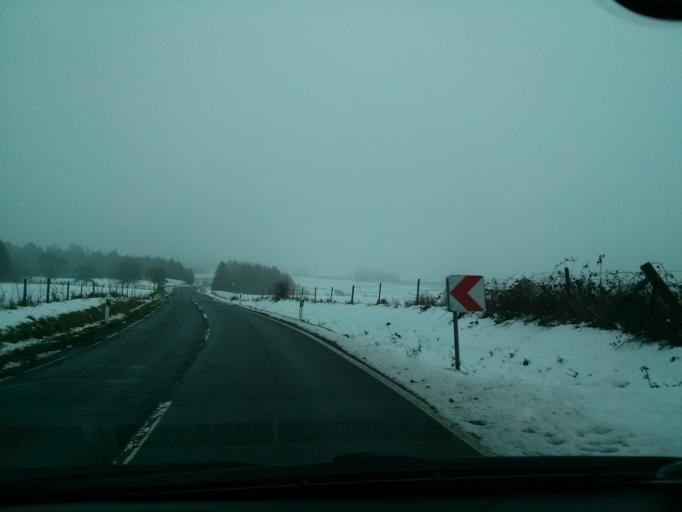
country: DE
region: Rheinland-Pfalz
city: Berg
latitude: 50.5661
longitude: 6.9570
